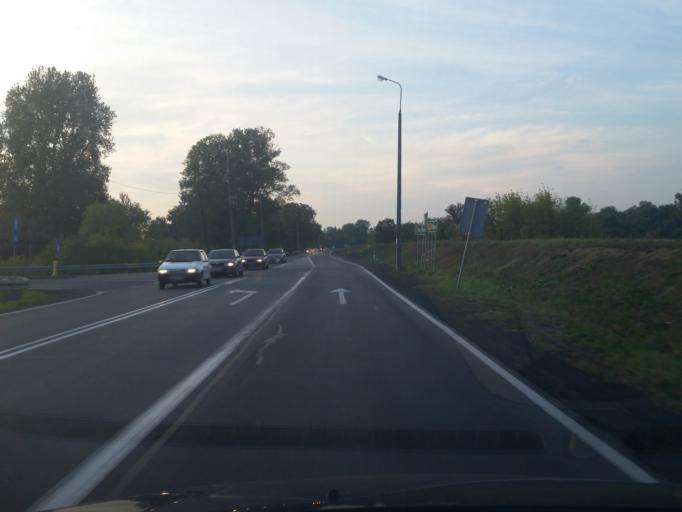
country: PL
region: Masovian Voivodeship
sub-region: Powiat nowodworski
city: Nowy Dwor Mazowiecki
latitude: 52.4142
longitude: 20.6939
